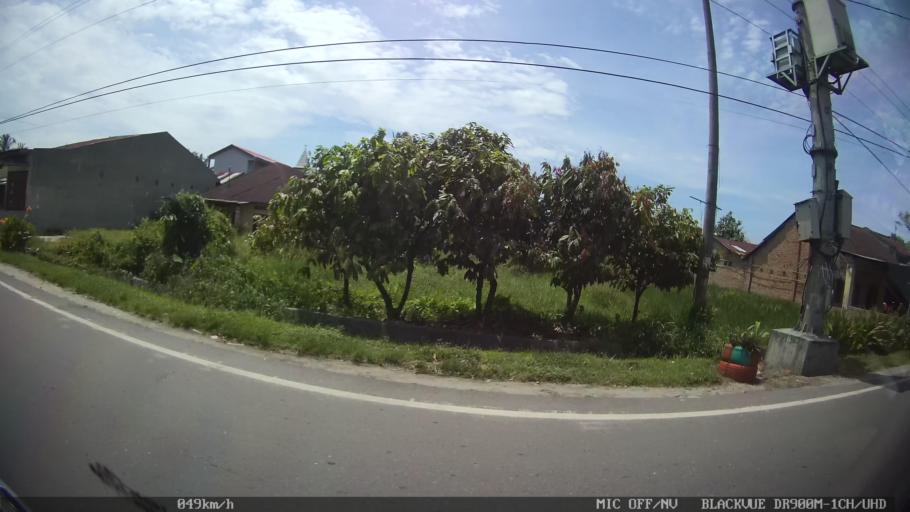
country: ID
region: North Sumatra
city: Percut
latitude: 3.5555
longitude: 98.8833
